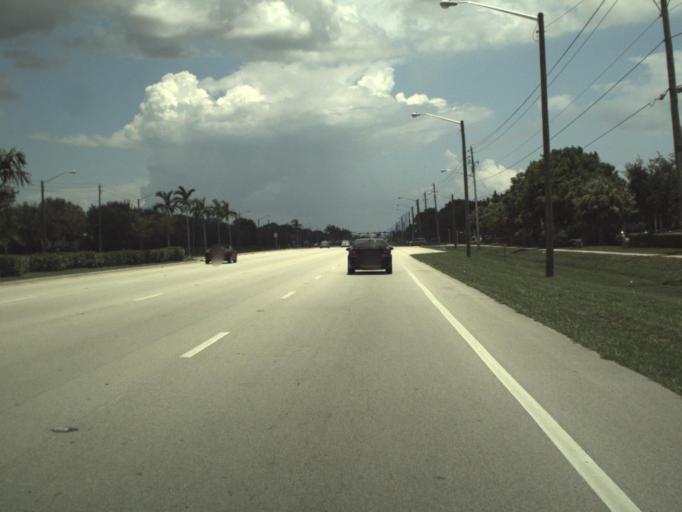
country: US
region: Florida
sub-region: Palm Beach County
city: Plantation Mobile Home Park
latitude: 26.7082
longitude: -80.1640
